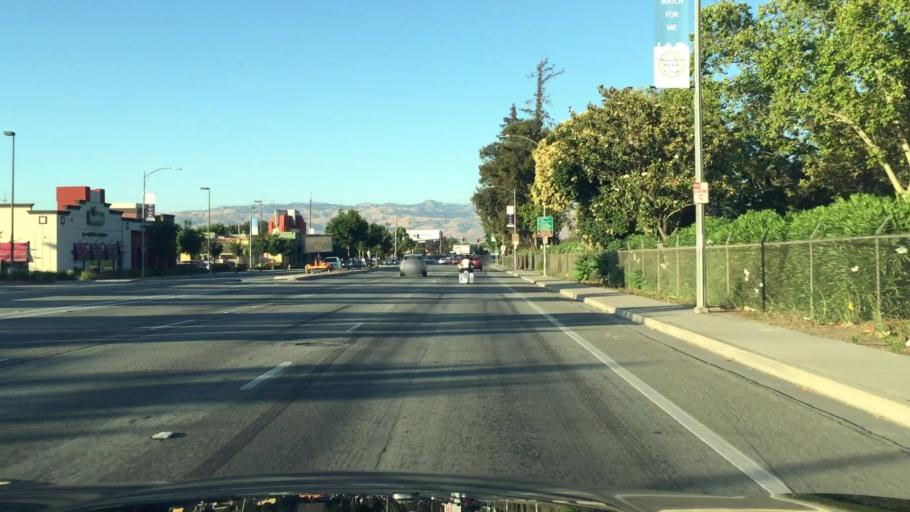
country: US
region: California
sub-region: Santa Clara County
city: Seven Trees
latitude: 37.3020
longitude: -121.8634
